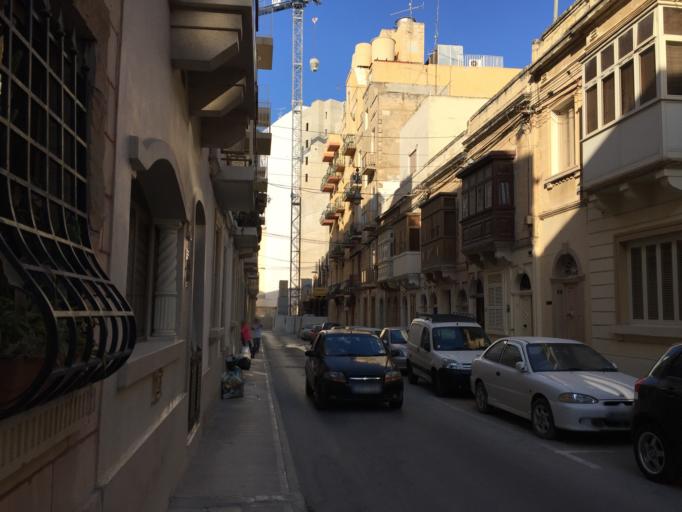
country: MT
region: Tas-Sliema
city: Sliema
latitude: 35.9074
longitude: 14.4971
